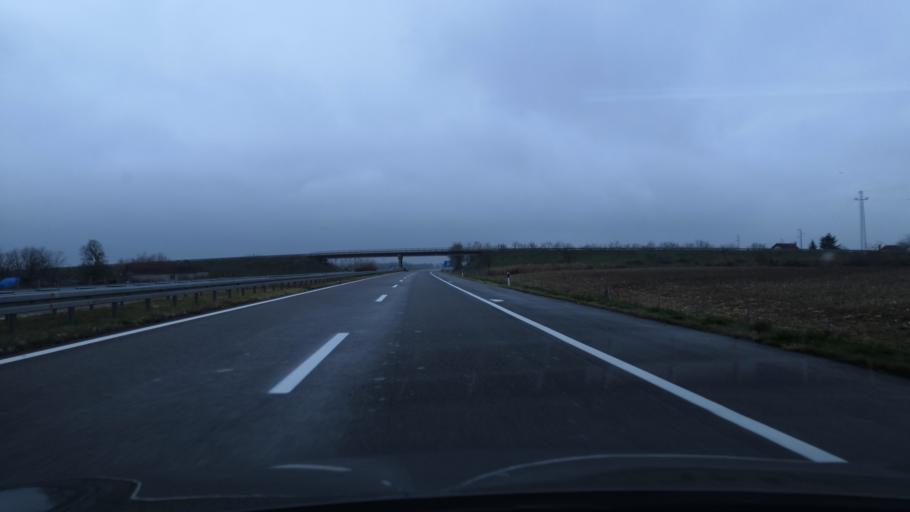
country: HU
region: Csongrad
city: Asotthalom
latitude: 46.0863
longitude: 19.7881
